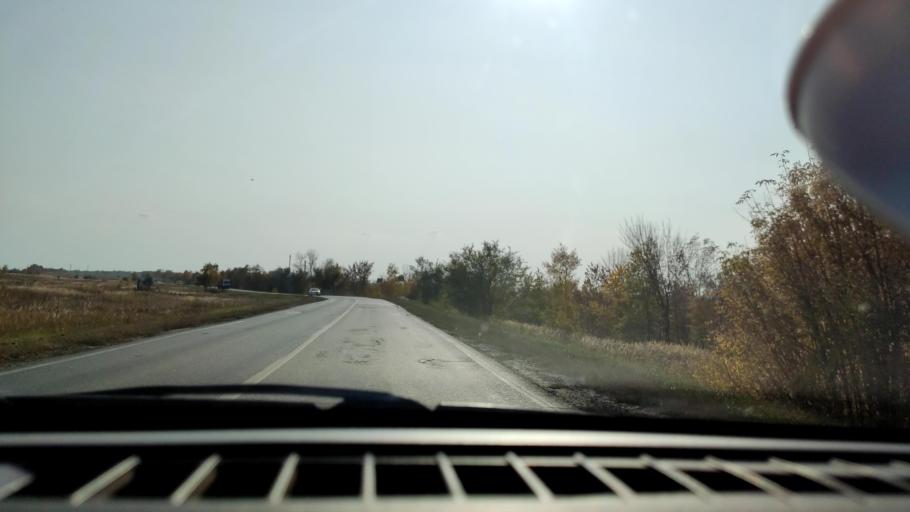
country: RU
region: Samara
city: Smyshlyayevka
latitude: 53.1065
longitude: 50.3507
